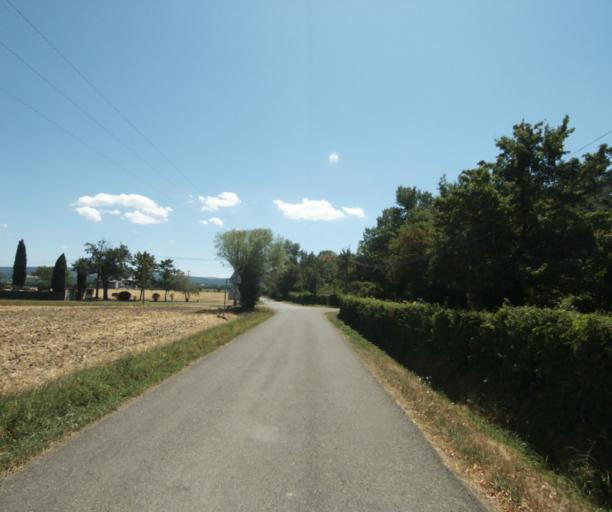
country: FR
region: Midi-Pyrenees
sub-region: Departement de la Haute-Garonne
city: Revel
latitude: 43.4574
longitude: 1.9478
